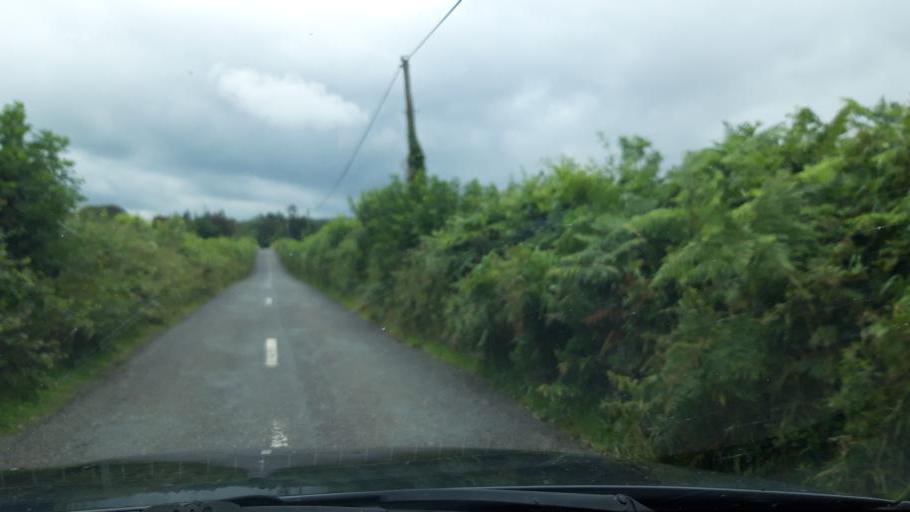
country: IE
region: Munster
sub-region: County Cork
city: Castlemartyr
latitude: 52.1338
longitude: -8.0103
